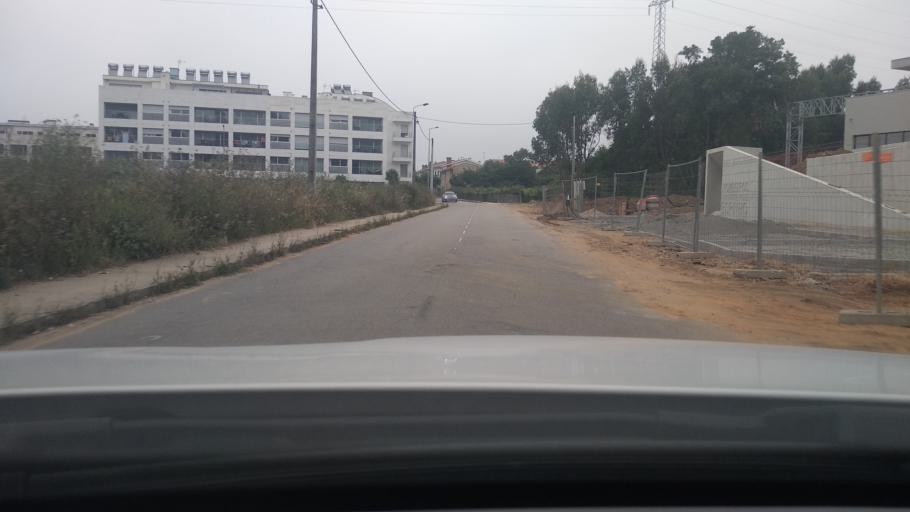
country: PT
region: Aveiro
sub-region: Espinho
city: Silvalde
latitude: 41.0012
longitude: -8.6275
